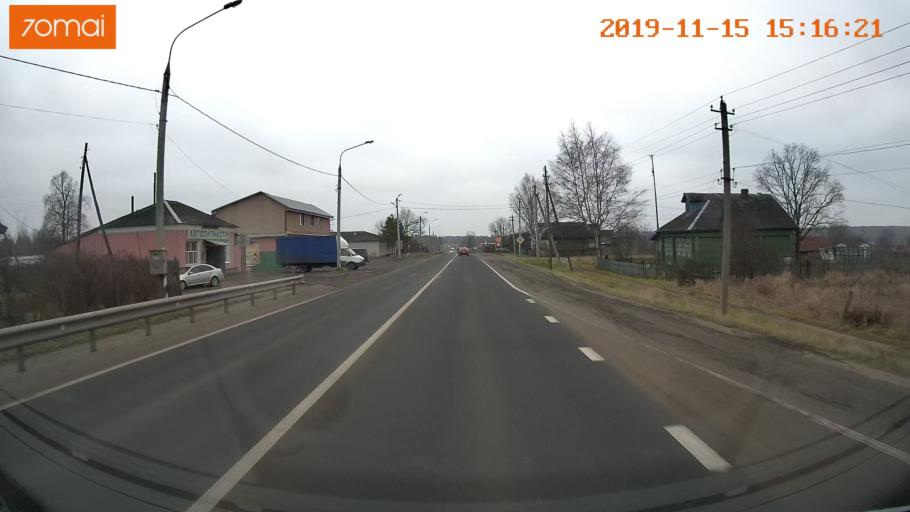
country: RU
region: Jaroslavl
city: Danilov
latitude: 58.2736
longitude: 40.1917
